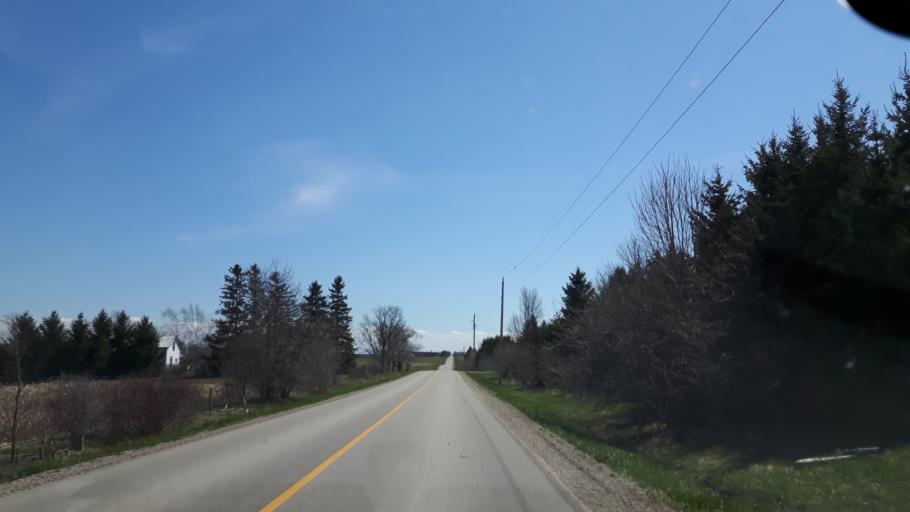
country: CA
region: Ontario
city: Goderich
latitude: 43.6535
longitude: -81.6441
